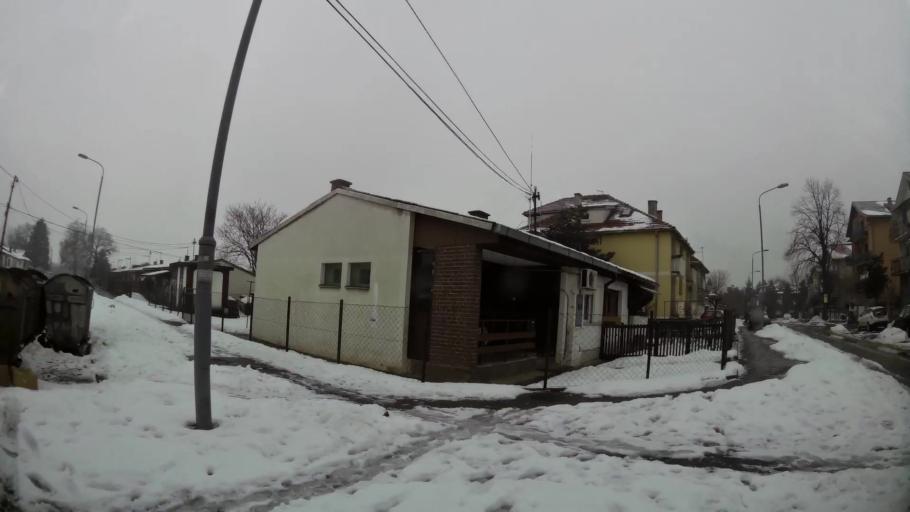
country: RS
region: Central Serbia
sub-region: Belgrade
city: Zemun
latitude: 44.8693
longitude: 20.3219
